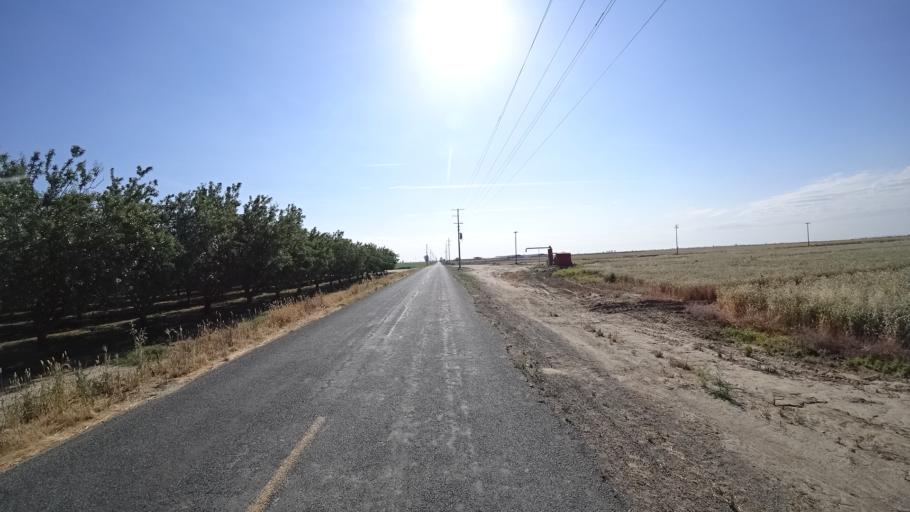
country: US
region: California
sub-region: Kings County
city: Armona
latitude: 36.2256
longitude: -119.7011
